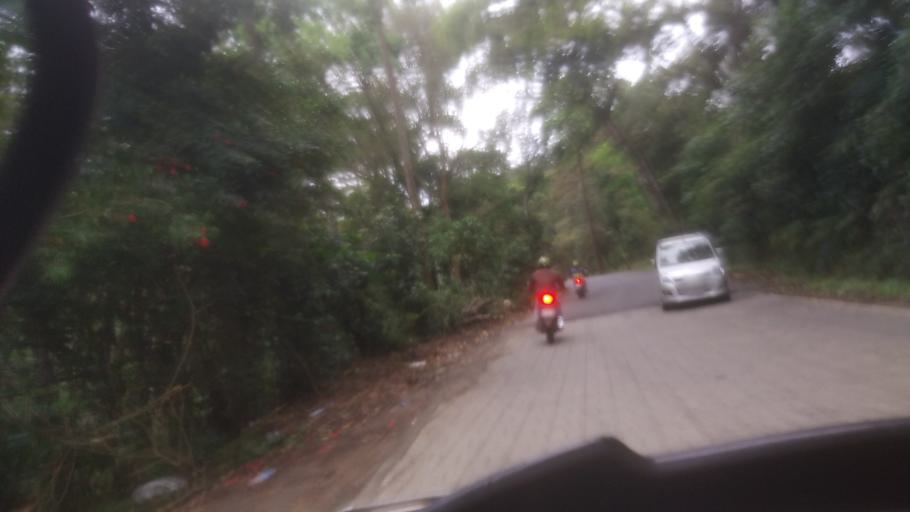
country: IN
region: Tamil Nadu
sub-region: Theni
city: Kombai
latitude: 9.8912
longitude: 77.1488
